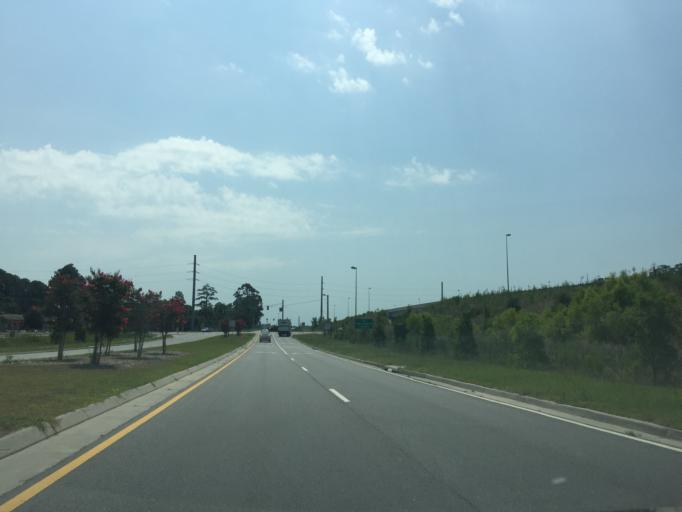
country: US
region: Georgia
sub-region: Chatham County
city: Montgomery
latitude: 31.9782
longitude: -81.1334
